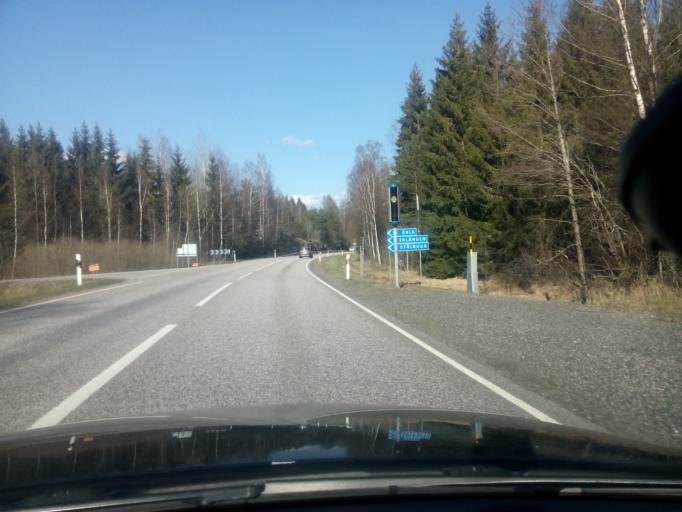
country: SE
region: Soedermanland
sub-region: Flens Kommun
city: Malmkoping
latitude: 59.2043
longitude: 16.7920
